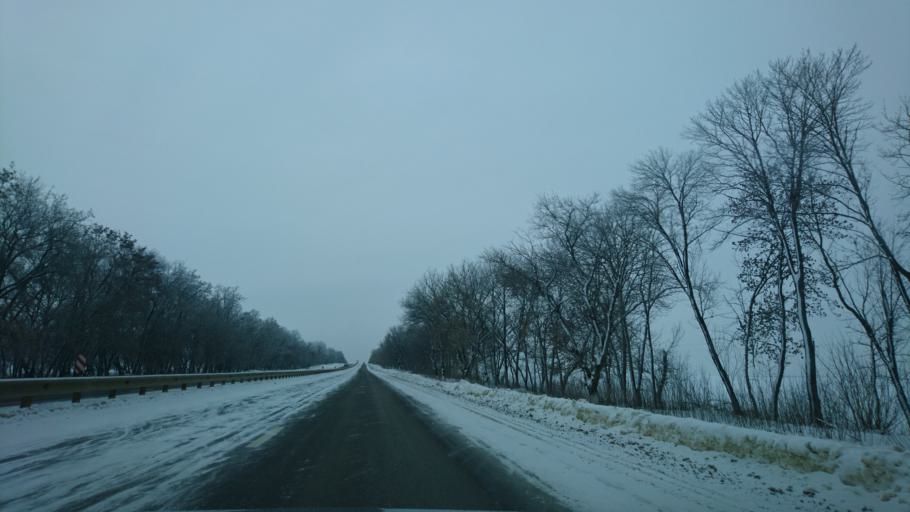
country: RU
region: Belgorod
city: Mayskiy
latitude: 50.4253
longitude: 36.3812
